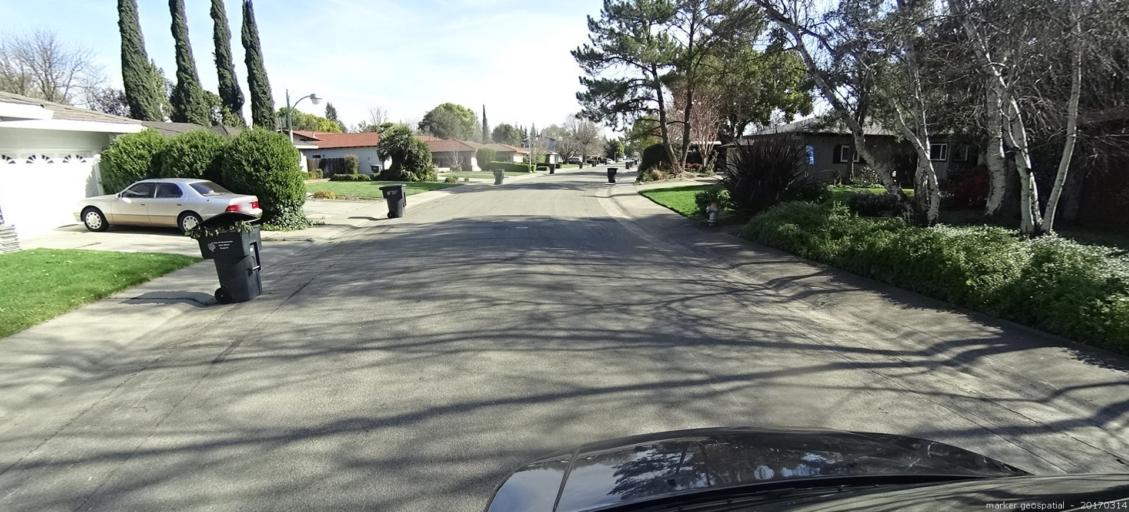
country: US
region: California
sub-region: Sacramento County
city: Parkway
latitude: 38.5049
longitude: -121.5253
